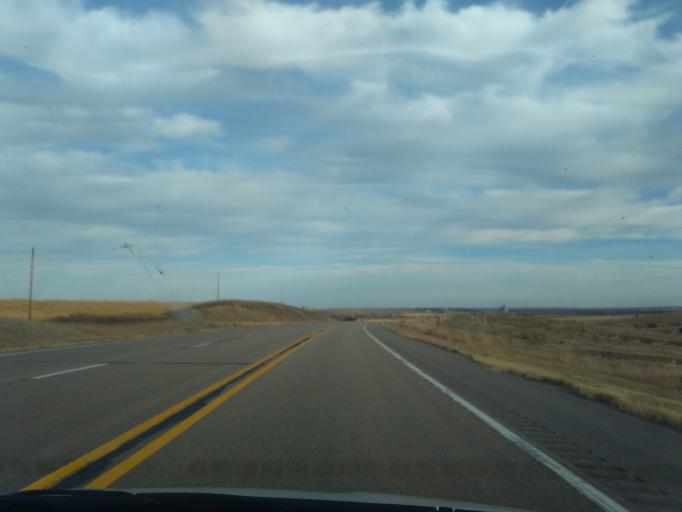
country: US
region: Nebraska
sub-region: Hitchcock County
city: Trenton
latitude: 40.2341
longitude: -100.9070
